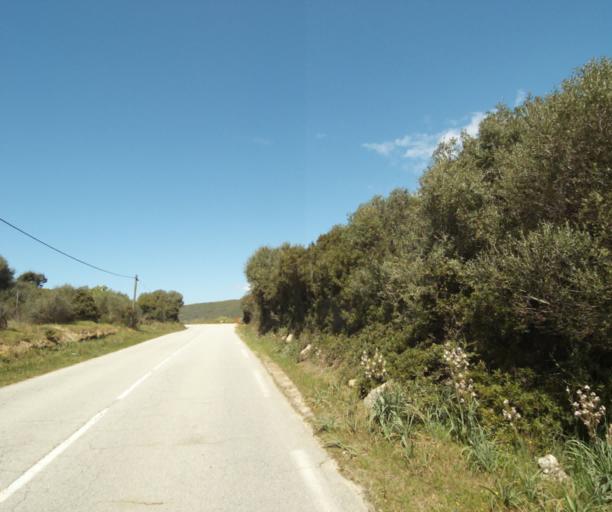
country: FR
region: Corsica
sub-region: Departement de la Corse-du-Sud
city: Propriano
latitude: 41.6582
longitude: 8.9003
